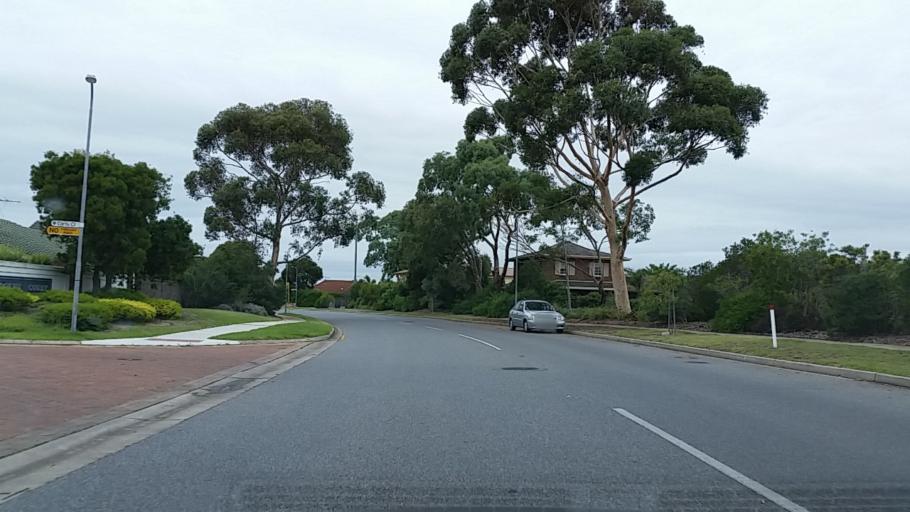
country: AU
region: South Australia
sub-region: Charles Sturt
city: West Lakes Shore
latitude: -34.8661
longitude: 138.4930
